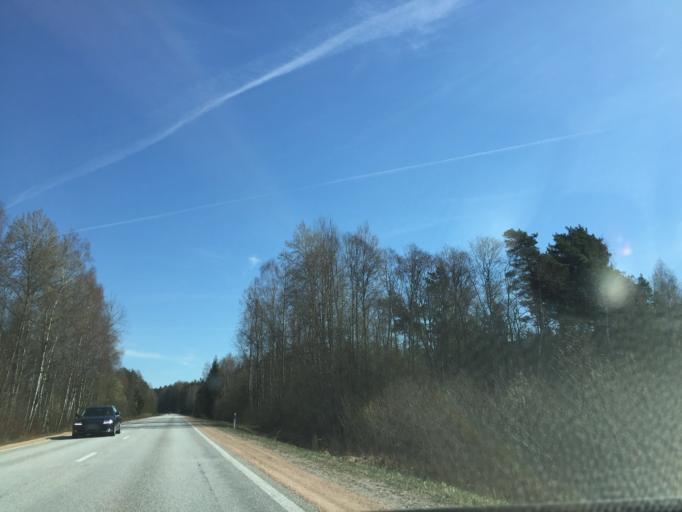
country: LV
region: Pargaujas
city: Stalbe
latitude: 57.3777
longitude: 25.0487
